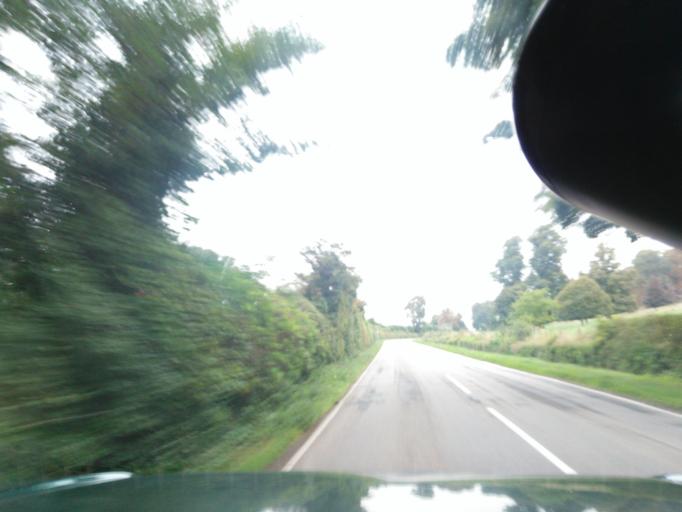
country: GB
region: England
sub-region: Dorset
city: Blandford Forum
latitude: 50.9073
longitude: -2.1936
